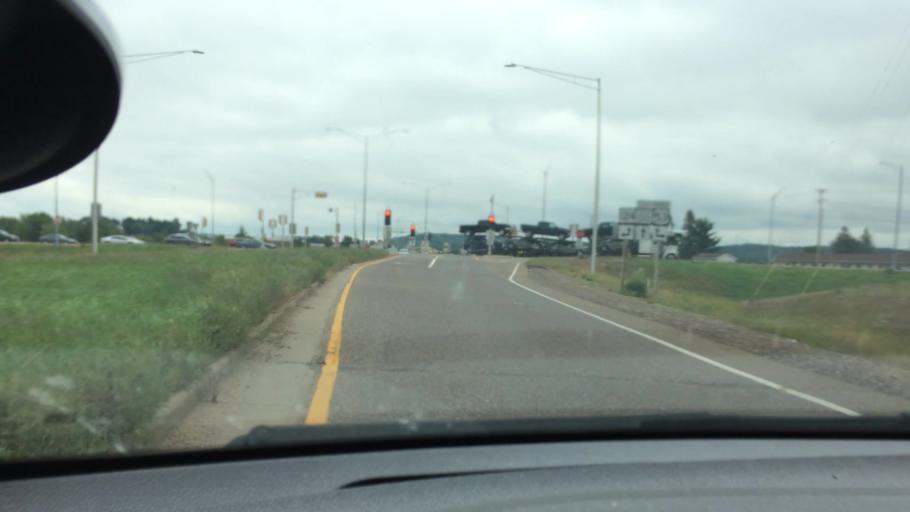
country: US
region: Wisconsin
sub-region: Chippewa County
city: Lake Hallie
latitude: 44.8874
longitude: -91.4248
